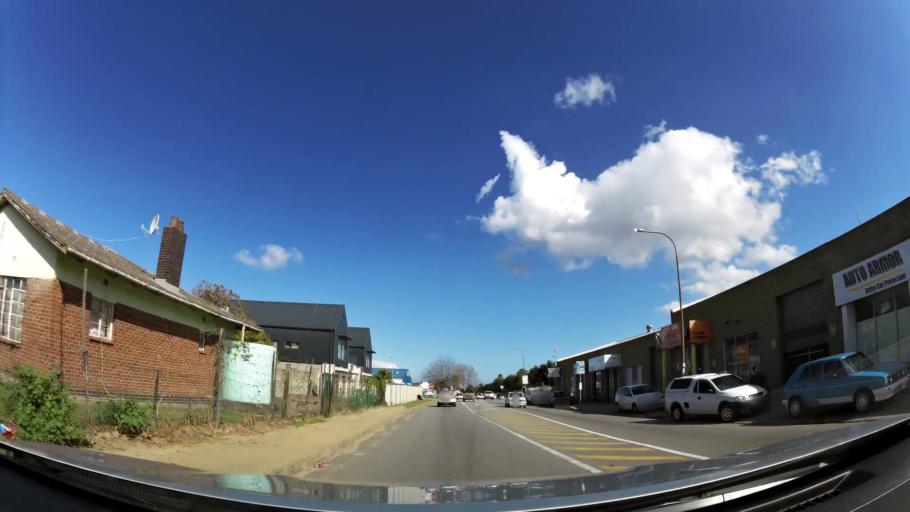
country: ZA
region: Western Cape
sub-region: Eden District Municipality
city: George
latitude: -33.9656
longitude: 22.4668
